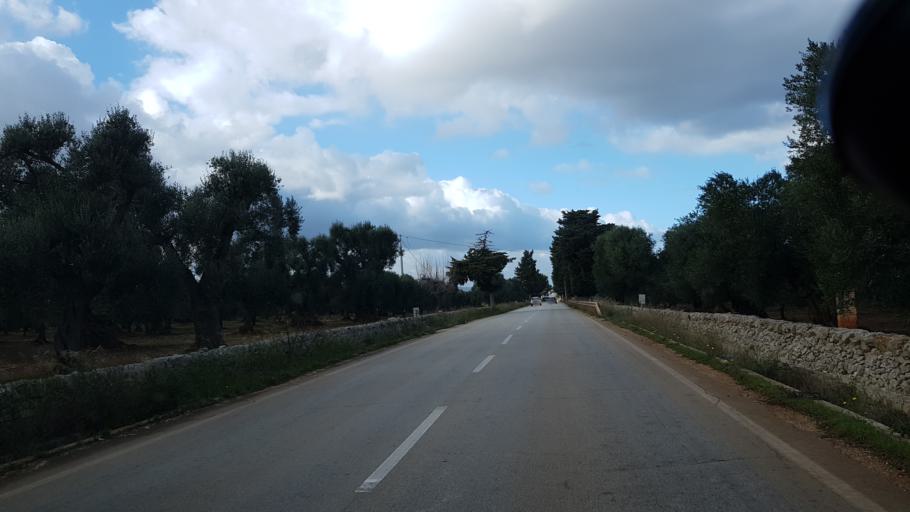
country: IT
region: Apulia
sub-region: Provincia di Brindisi
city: Montalbano
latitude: 40.7753
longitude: 17.4960
